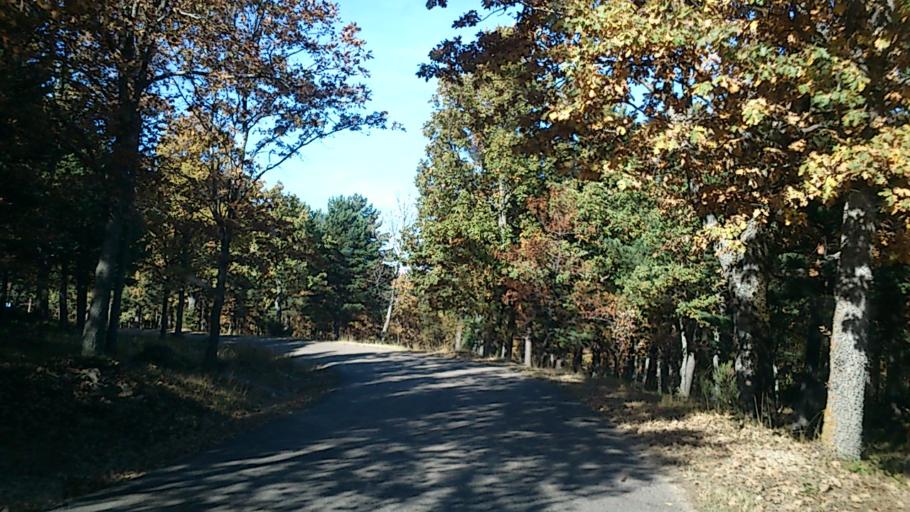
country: ES
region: Aragon
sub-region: Provincia de Zaragoza
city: Litago
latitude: 41.8062
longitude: -1.7932
